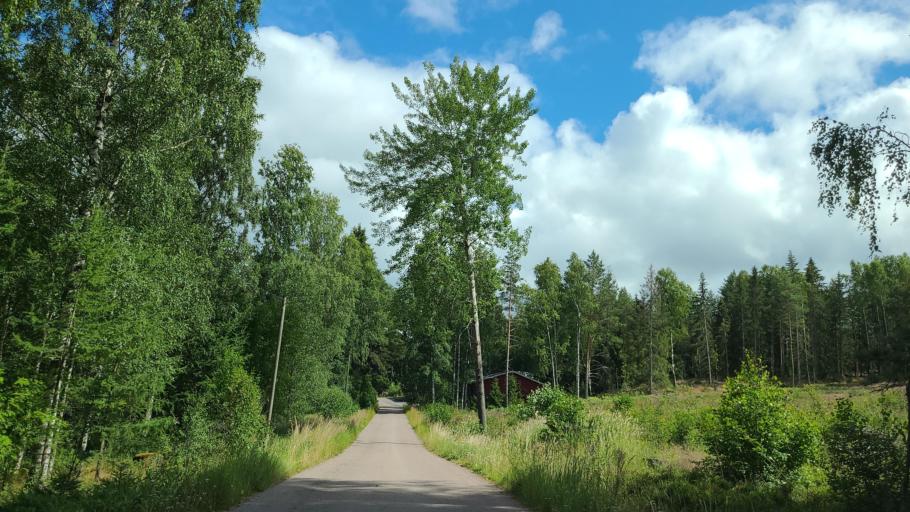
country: FI
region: Varsinais-Suomi
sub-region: Aboland-Turunmaa
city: Nagu
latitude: 60.1810
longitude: 22.0570
